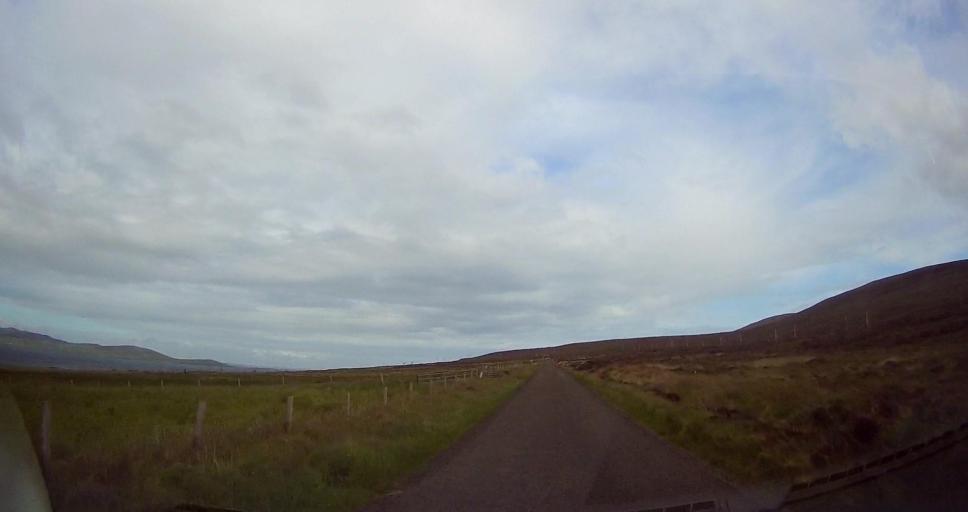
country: GB
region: Scotland
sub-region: Orkney Islands
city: Stromness
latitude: 58.9031
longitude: -3.3011
